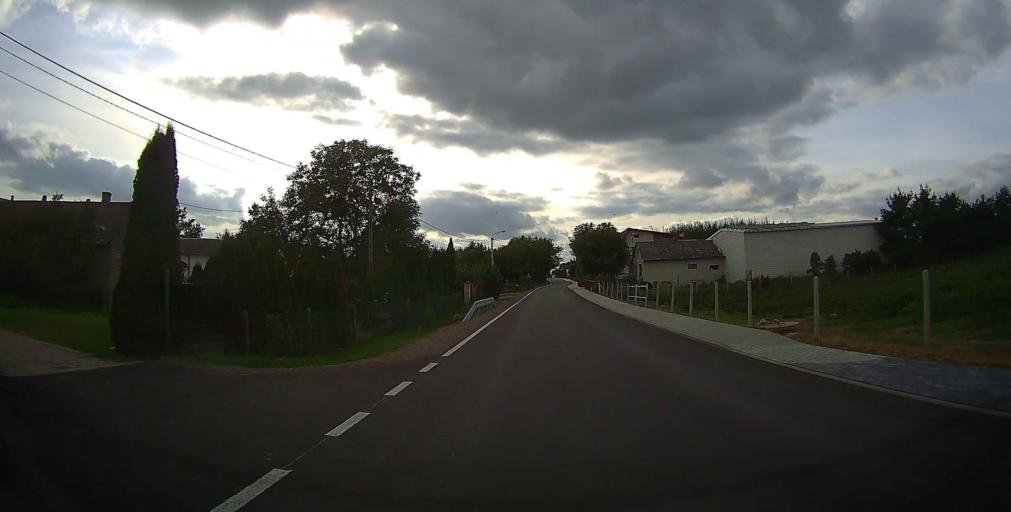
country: PL
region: Masovian Voivodeship
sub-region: Powiat bialobrzeski
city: Promna
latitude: 51.7083
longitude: 20.9533
